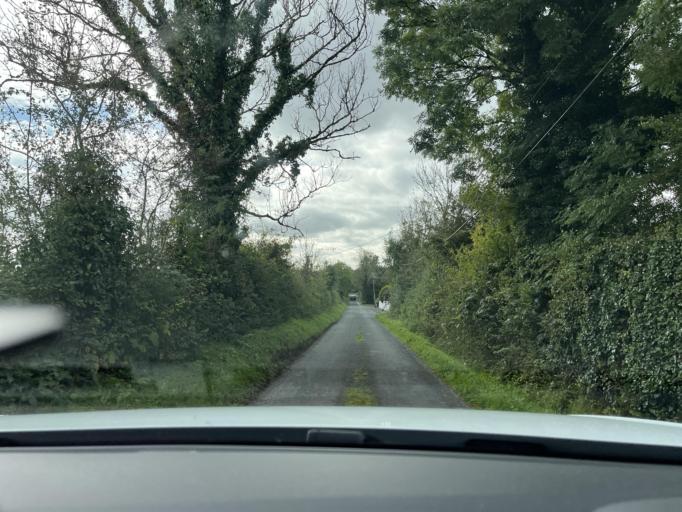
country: IE
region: Connaught
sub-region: County Leitrim
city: Carrick-on-Shannon
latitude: 53.9641
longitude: -8.0850
